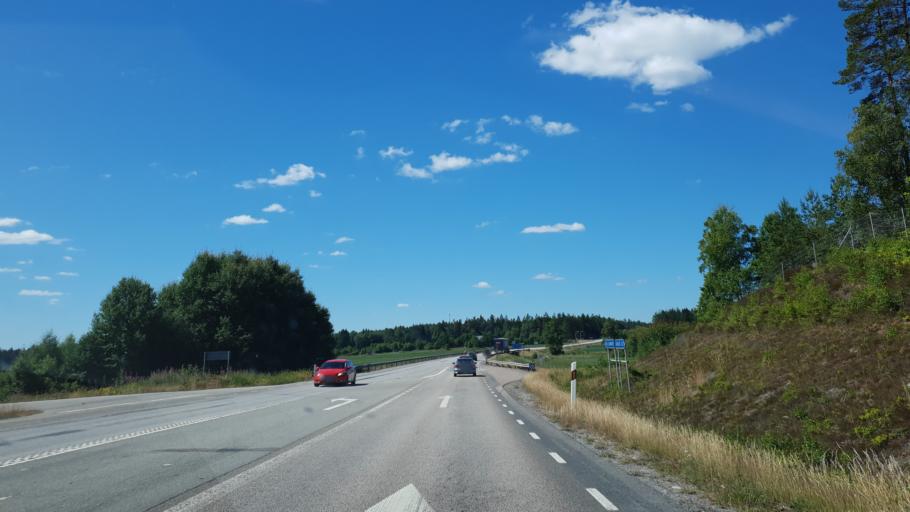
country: SE
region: Kronoberg
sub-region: Alvesta Kommun
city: Alvesta
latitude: 56.9086
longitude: 14.4742
